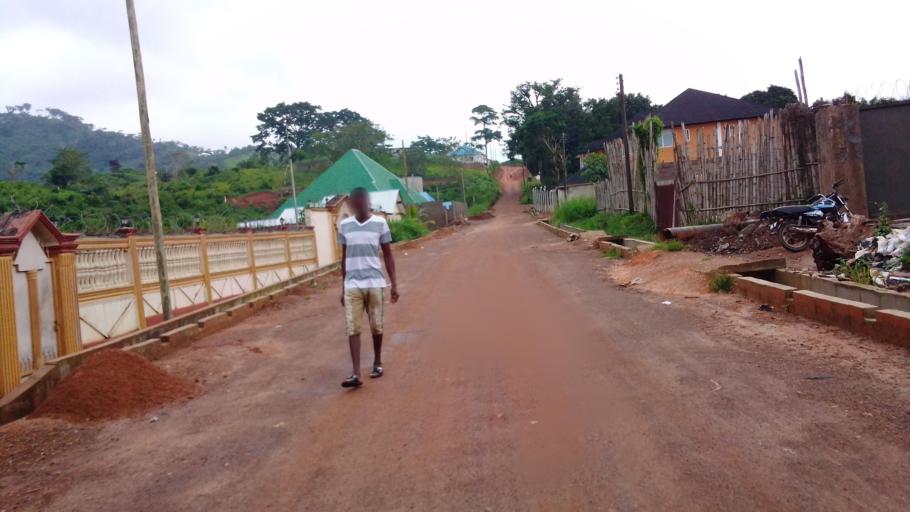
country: SL
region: Eastern Province
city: Kenema
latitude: 7.8912
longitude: -11.1912
